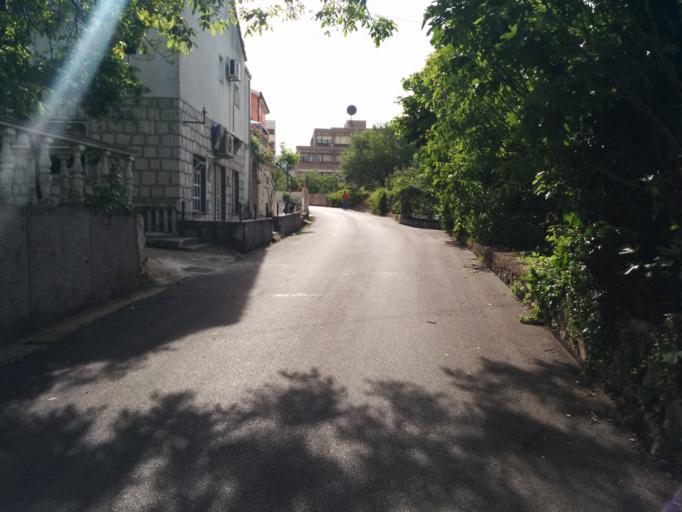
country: HR
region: Splitsko-Dalmatinska
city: Sinj
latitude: 43.7019
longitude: 16.6408
